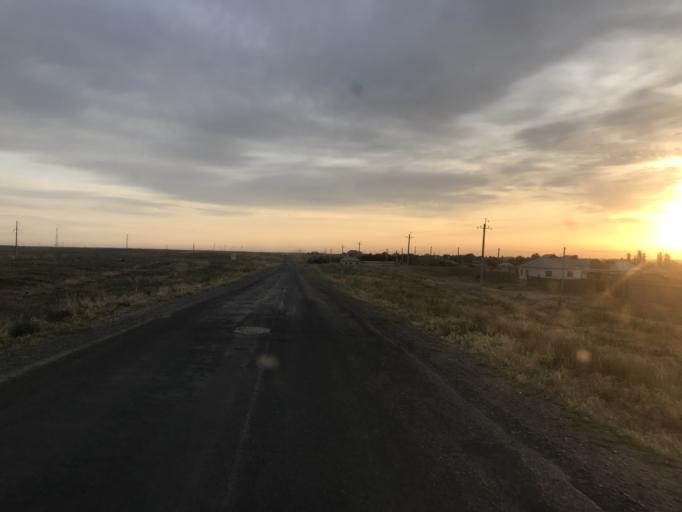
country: UZ
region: Toshkent
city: Amir Timur
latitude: 41.2302
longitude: 68.8079
